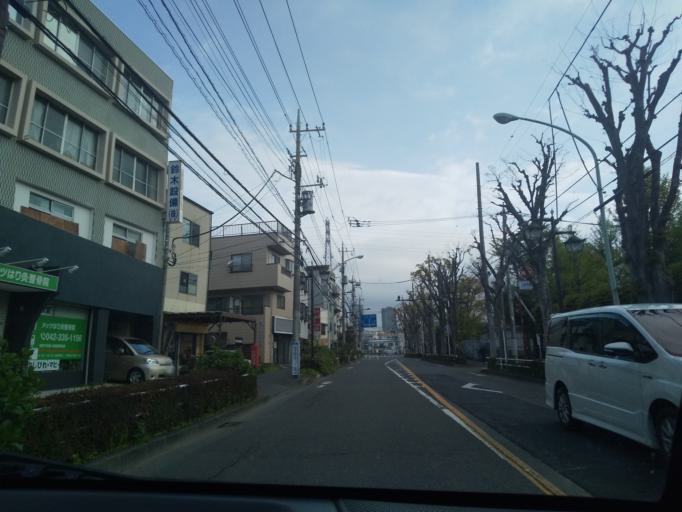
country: JP
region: Tokyo
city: Kokubunji
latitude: 35.6874
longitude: 139.4797
